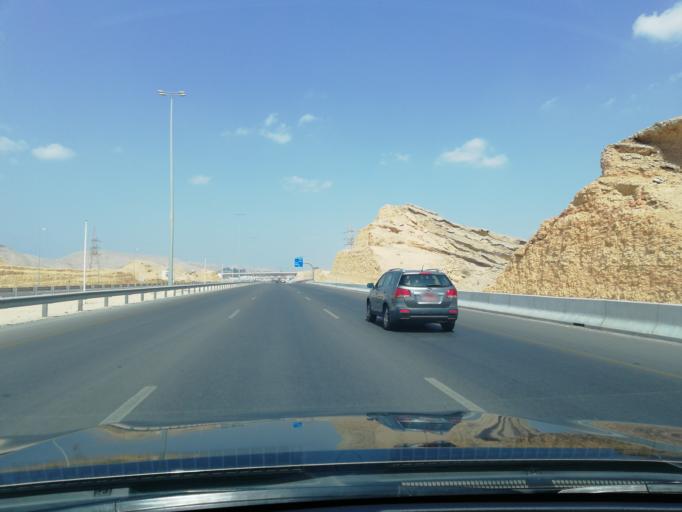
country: OM
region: Muhafazat Masqat
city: As Sib al Jadidah
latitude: 23.5659
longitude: 58.1982
